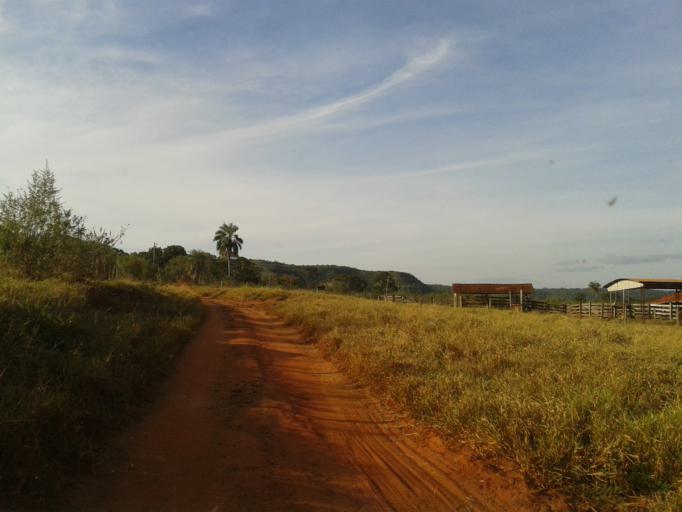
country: BR
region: Minas Gerais
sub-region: Campina Verde
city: Campina Verde
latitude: -19.5065
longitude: -49.6063
